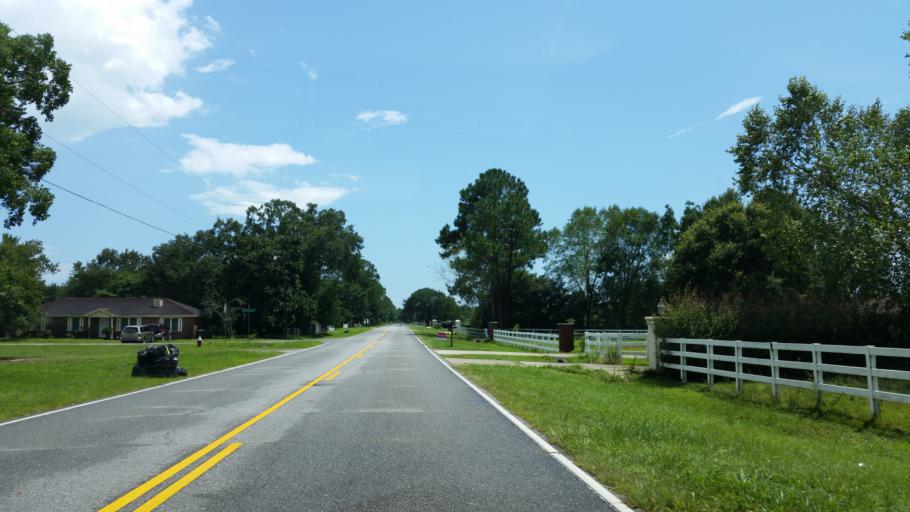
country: US
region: Florida
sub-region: Escambia County
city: Ensley
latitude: 30.5386
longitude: -87.3005
